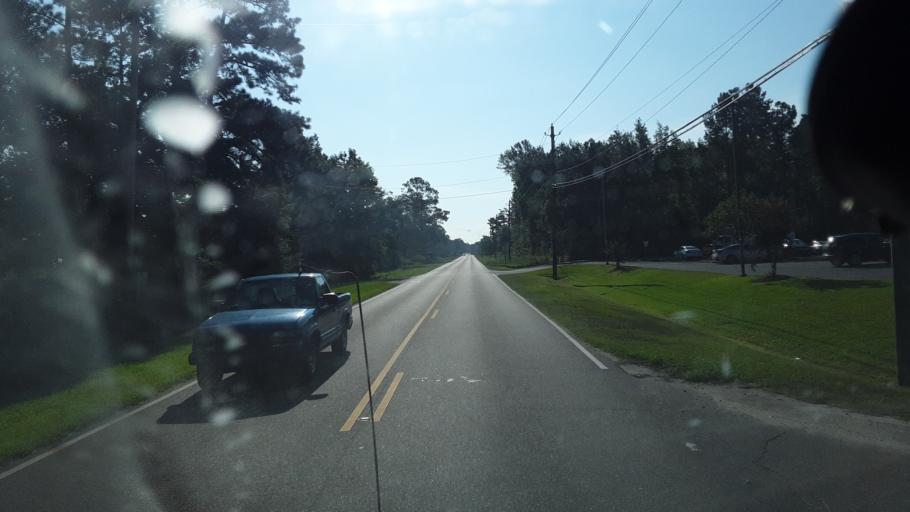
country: US
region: North Carolina
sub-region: Brunswick County
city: Leland
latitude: 34.2497
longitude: -78.0327
